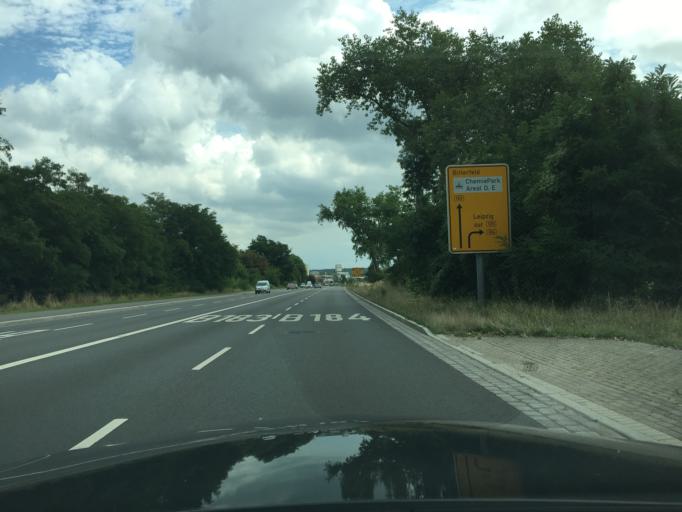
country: DE
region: Saxony-Anhalt
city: Sandersdorf
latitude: 51.6237
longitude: 12.2833
